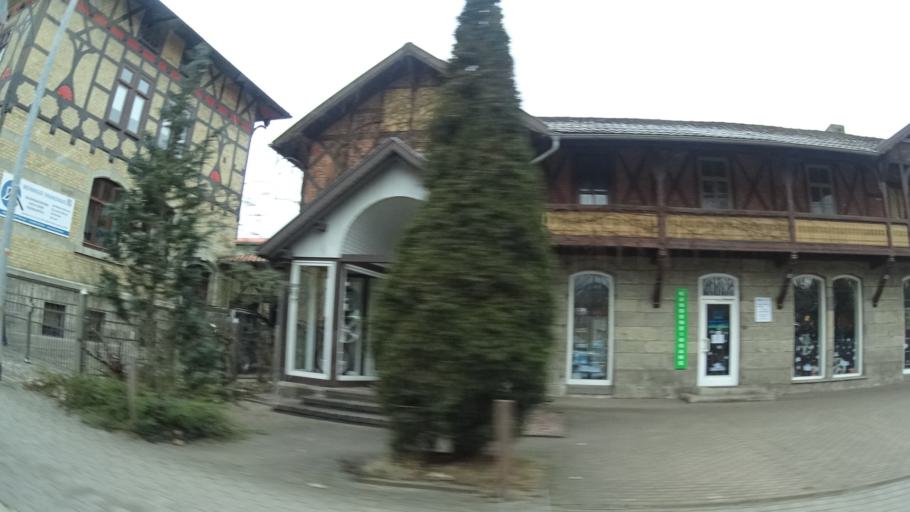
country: DE
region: Thuringia
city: Meiningen
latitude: 50.5632
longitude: 10.4148
